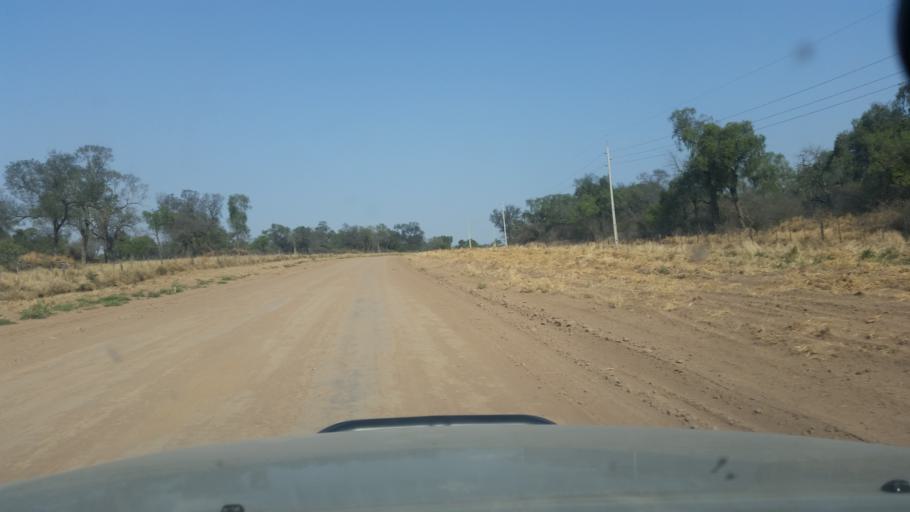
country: PY
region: Boqueron
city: Filadelfia
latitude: -22.0744
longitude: -60.6897
